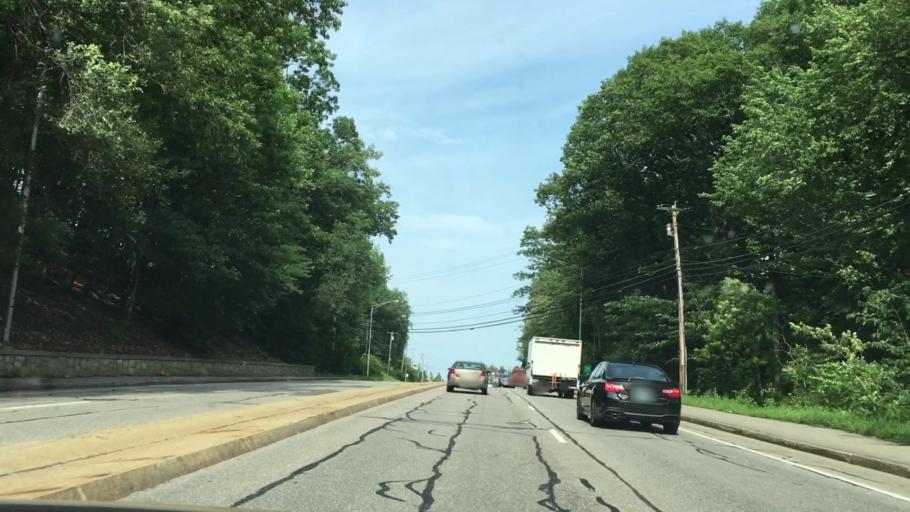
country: US
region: New Hampshire
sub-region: Merrimack County
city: Concord
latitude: 43.2102
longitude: -71.5218
